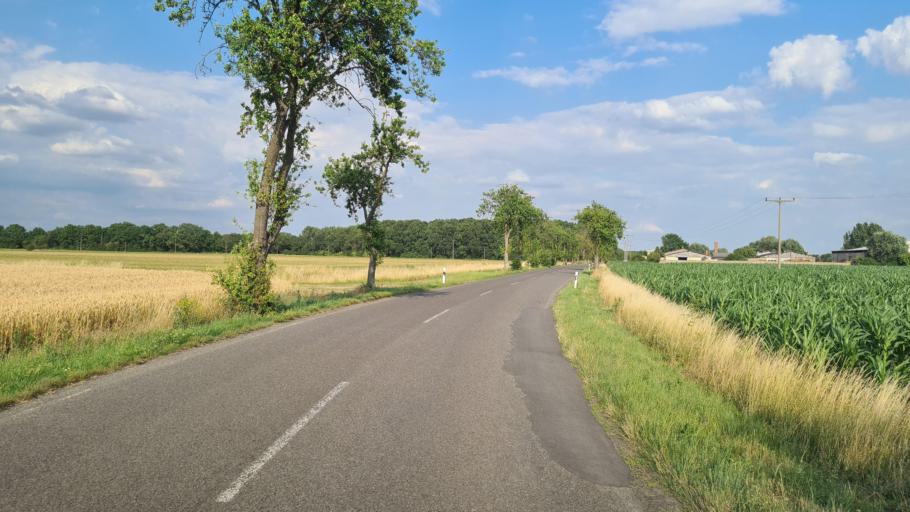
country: DE
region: Saxony-Anhalt
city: Pretzsch
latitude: 51.7579
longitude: 12.8705
